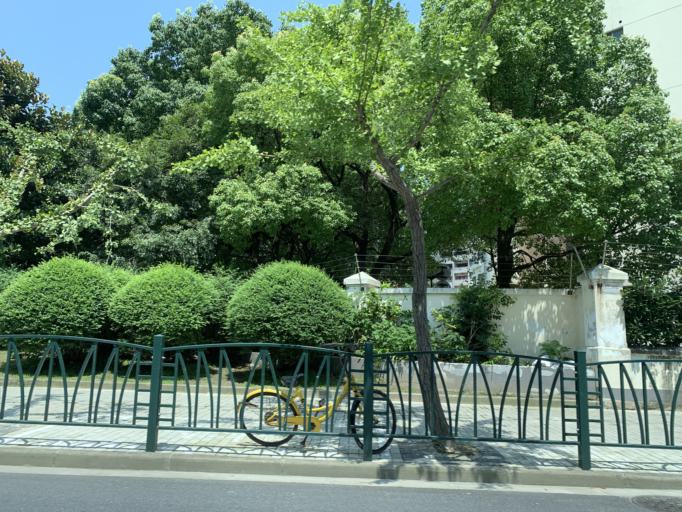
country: CN
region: Shanghai Shi
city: Huamu
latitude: 31.2060
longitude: 121.5144
